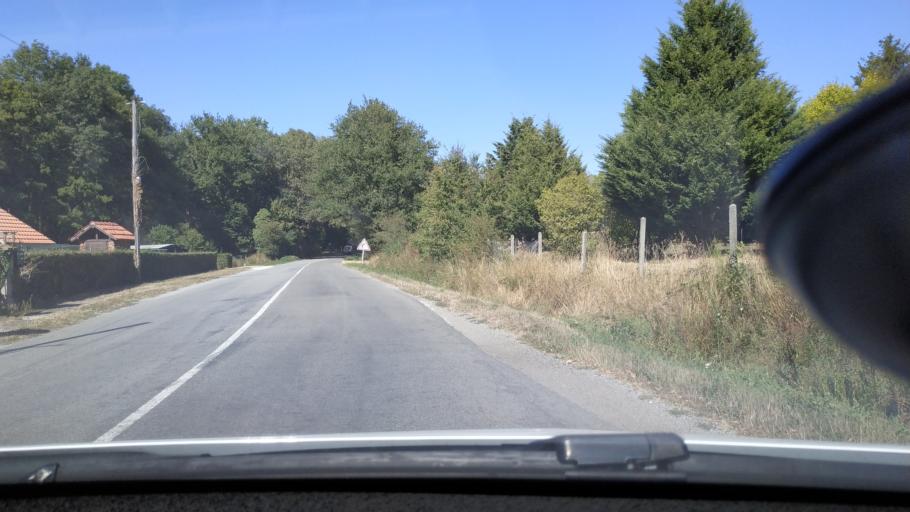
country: FR
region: Centre
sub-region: Departement du Loiret
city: Coullons
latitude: 47.6235
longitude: 2.5018
